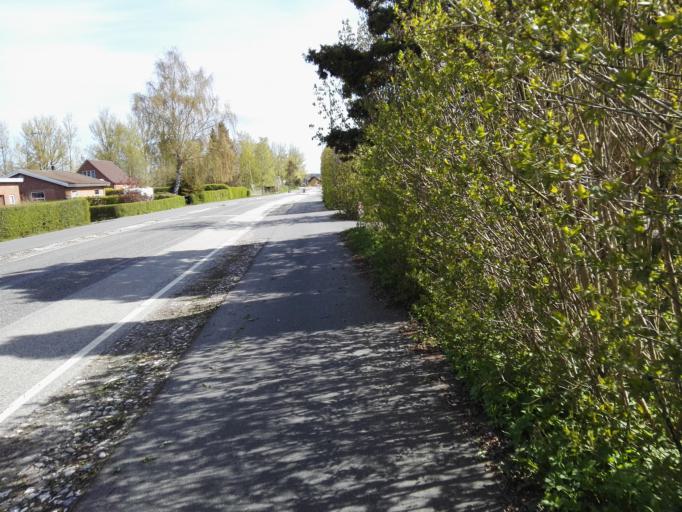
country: DK
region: Capital Region
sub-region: Halsnaes Kommune
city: Frederiksvaerk
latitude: 55.9720
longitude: 11.9963
